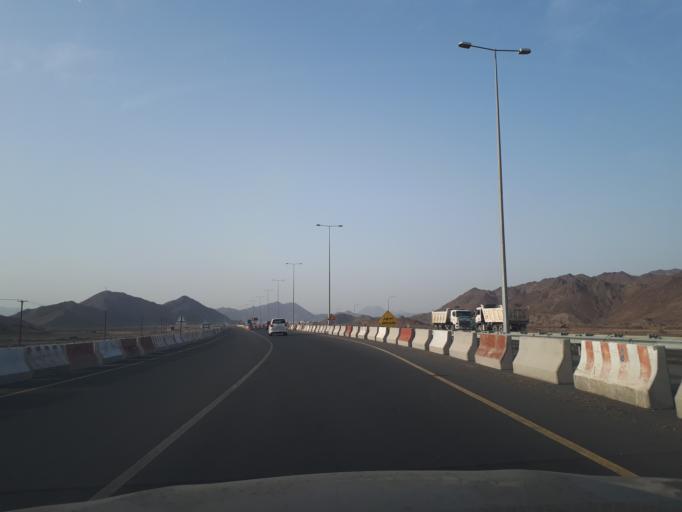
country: OM
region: Muhafazat ad Dakhiliyah
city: Sufalat Sama'il
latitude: 23.2917
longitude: 58.1096
